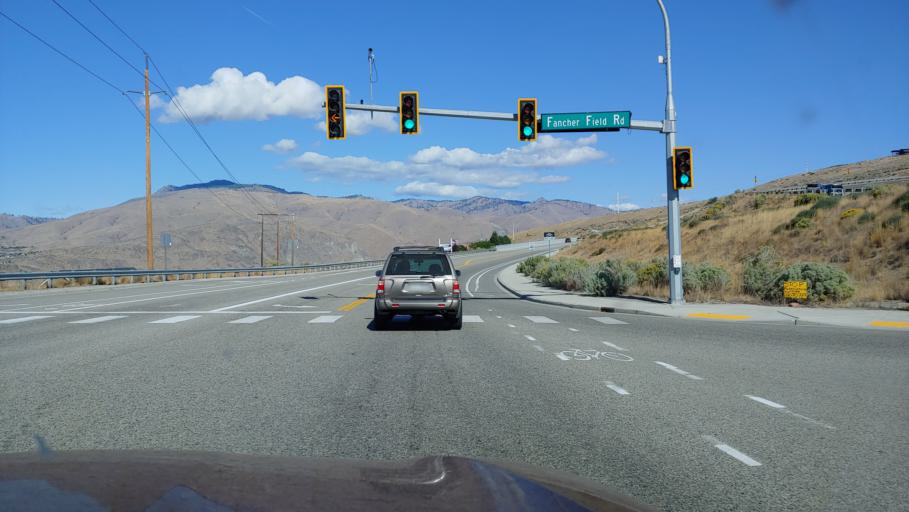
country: US
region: Washington
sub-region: Douglas County
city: East Wenatchee Bench
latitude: 47.4553
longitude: -120.2922
